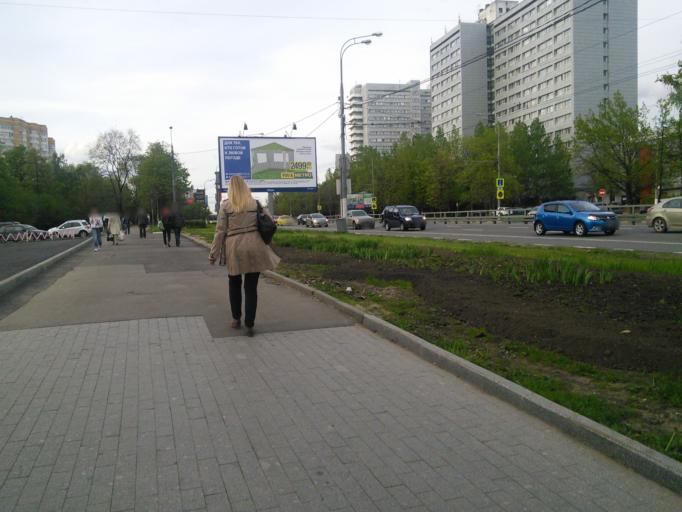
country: RU
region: Moscow
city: Yasenevo
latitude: 55.6444
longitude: 37.5270
